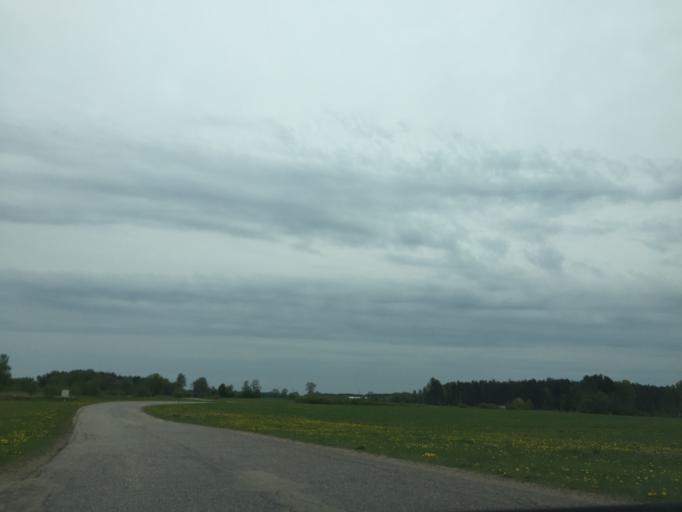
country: LV
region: Garkalne
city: Garkalne
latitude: 57.0637
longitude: 24.3823
